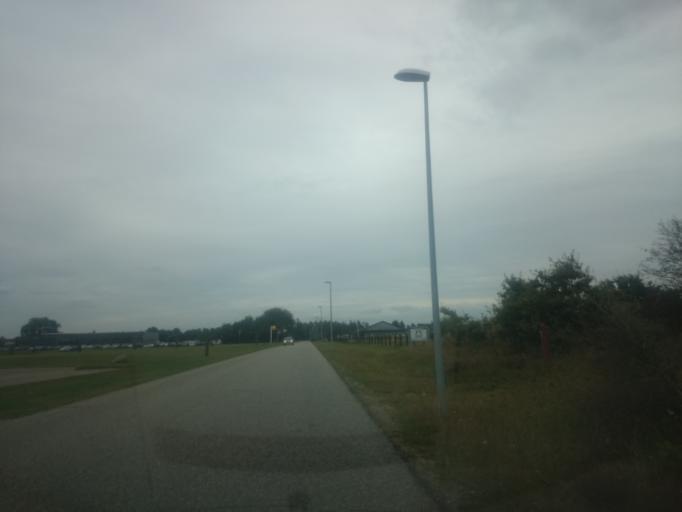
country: DK
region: South Denmark
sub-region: Billund Kommune
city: Grindsted
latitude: 55.7528
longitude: 8.9605
